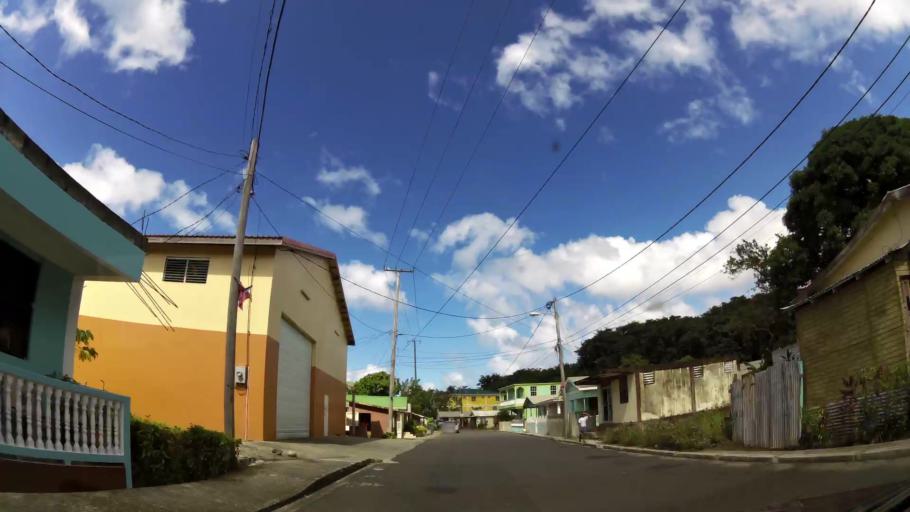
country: DM
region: Saint John
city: Portsmouth
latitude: 15.5808
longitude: -61.4593
